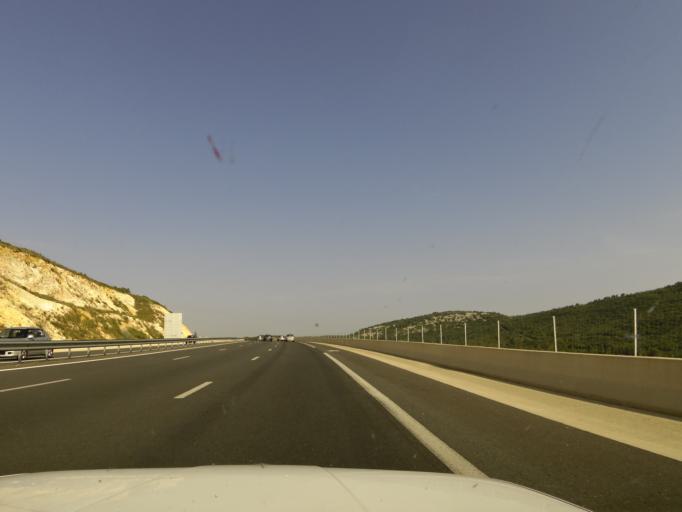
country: FR
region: Languedoc-Roussillon
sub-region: Departement de l'Herault
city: Gignac
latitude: 43.6277
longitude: 3.5953
